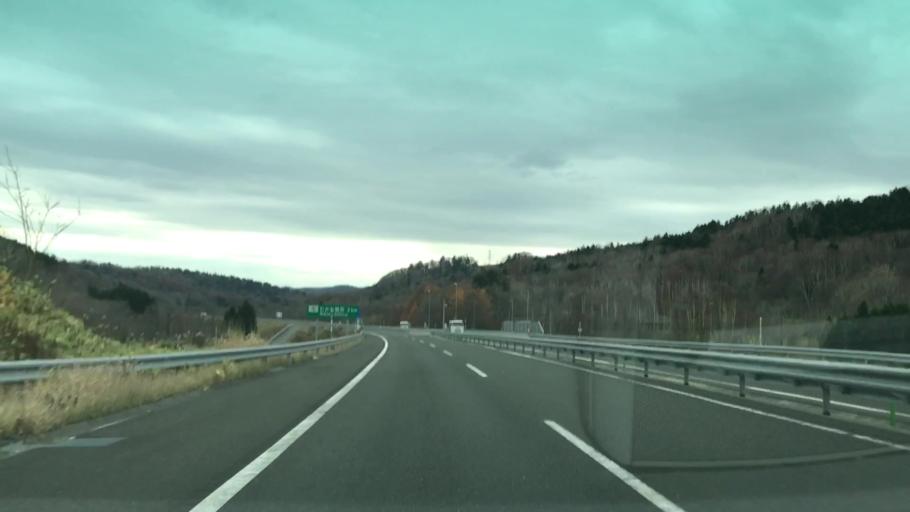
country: JP
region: Hokkaido
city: Shimo-furano
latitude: 42.9362
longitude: 142.2077
